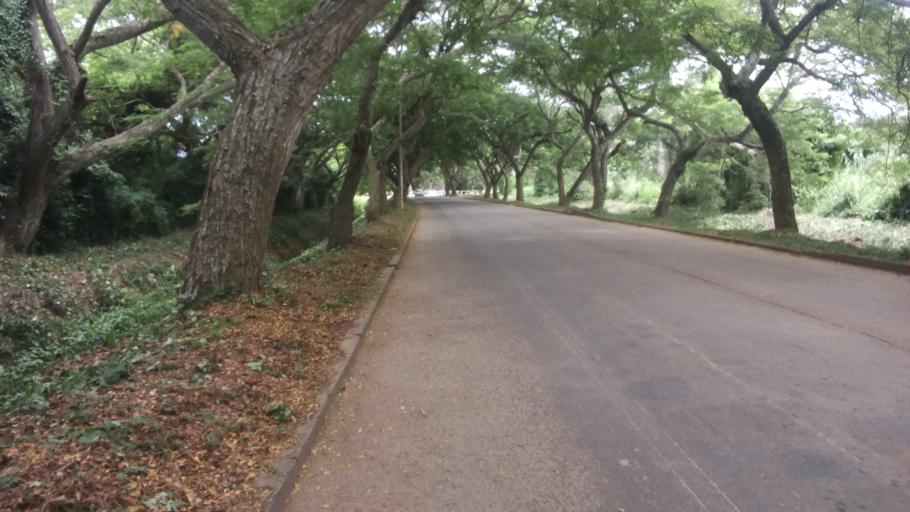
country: GH
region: Central
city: Cape Coast
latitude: 5.1193
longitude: -1.2870
